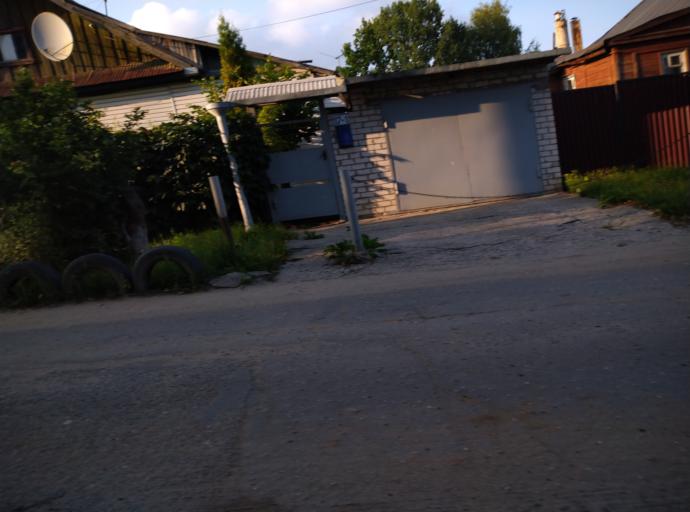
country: RU
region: Kostroma
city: Oktyabr'skiy
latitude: 57.7504
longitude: 40.9691
